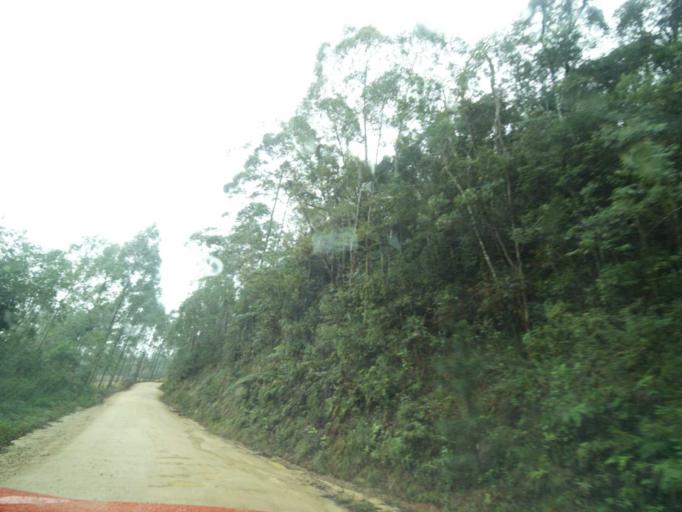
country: BR
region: Santa Catarina
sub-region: Anitapolis
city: Anitapolis
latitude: -27.9201
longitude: -49.1754
